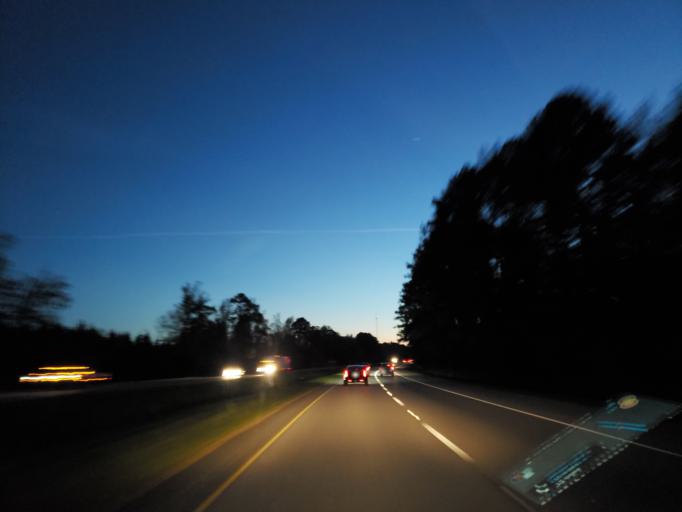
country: US
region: Mississippi
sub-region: Clarke County
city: Stonewall
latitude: 32.2181
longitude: -88.8346
